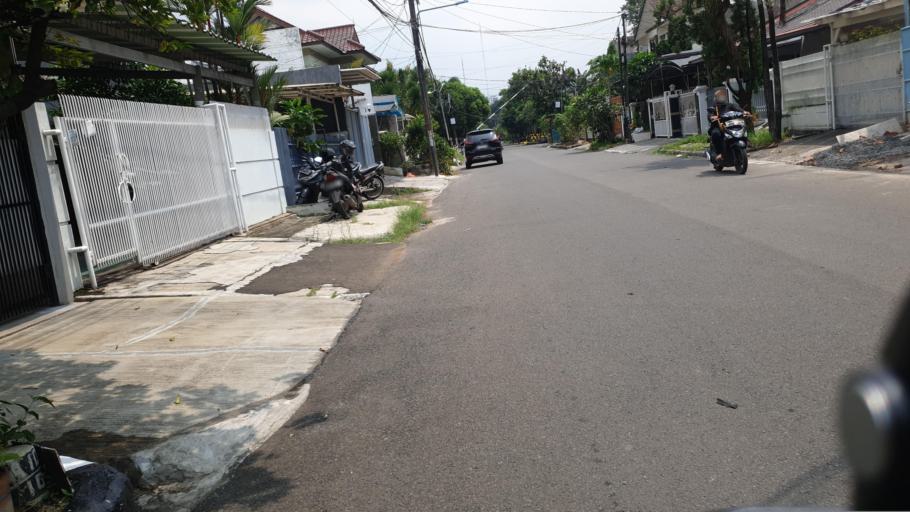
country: ID
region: West Java
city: Ciputat
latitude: -6.1954
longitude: 106.7452
